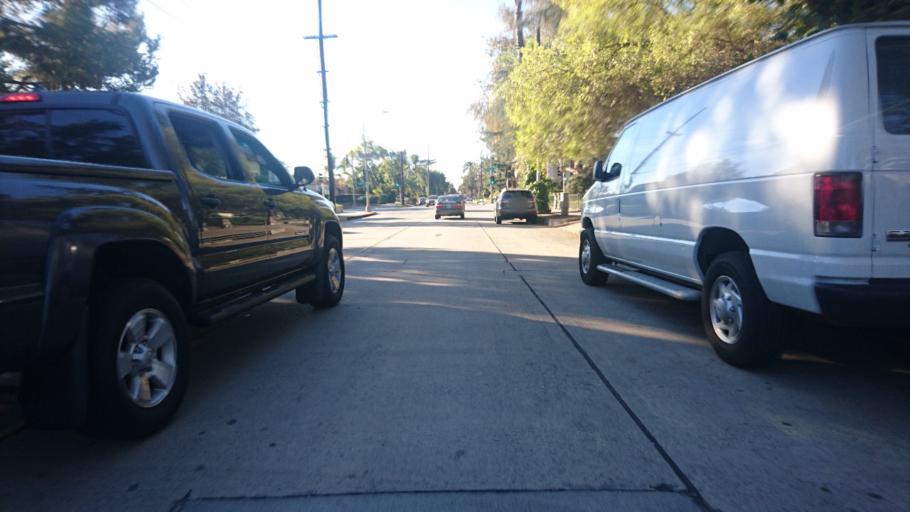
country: US
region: California
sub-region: Los Angeles County
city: East Pasadena
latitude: 34.1428
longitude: -118.0988
